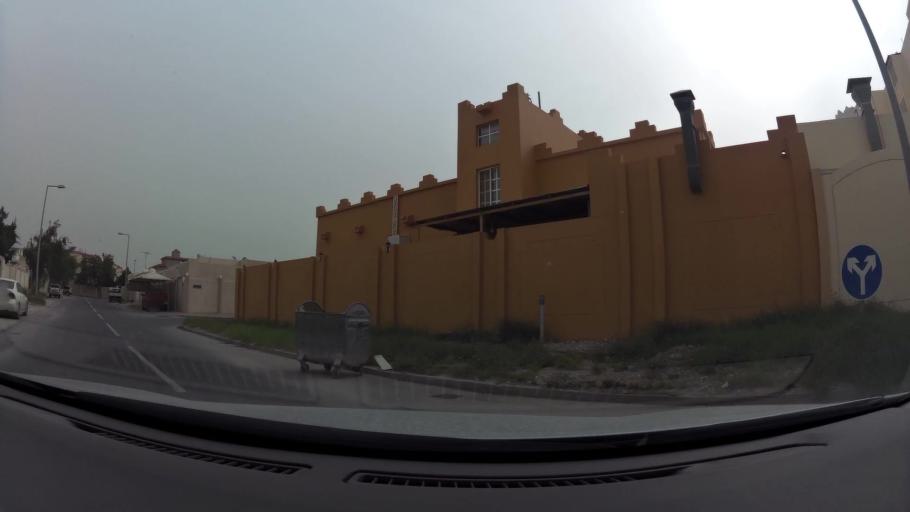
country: QA
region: Baladiyat ad Dawhah
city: Doha
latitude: 25.2475
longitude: 51.5155
